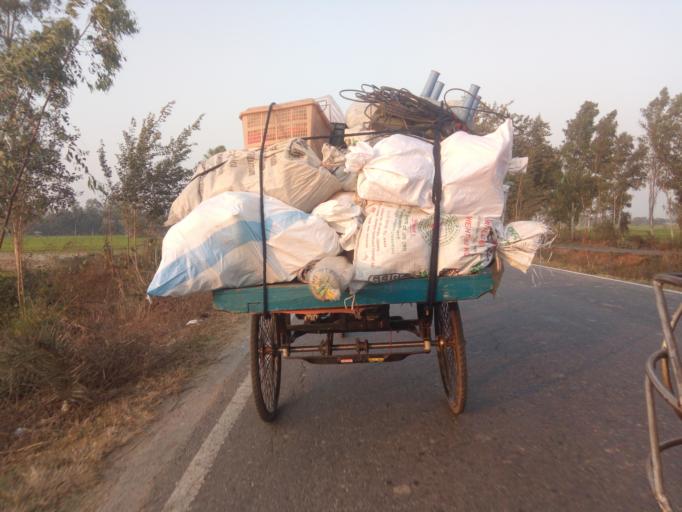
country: BD
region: Rajshahi
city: Bogra
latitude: 24.6000
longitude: 89.2391
